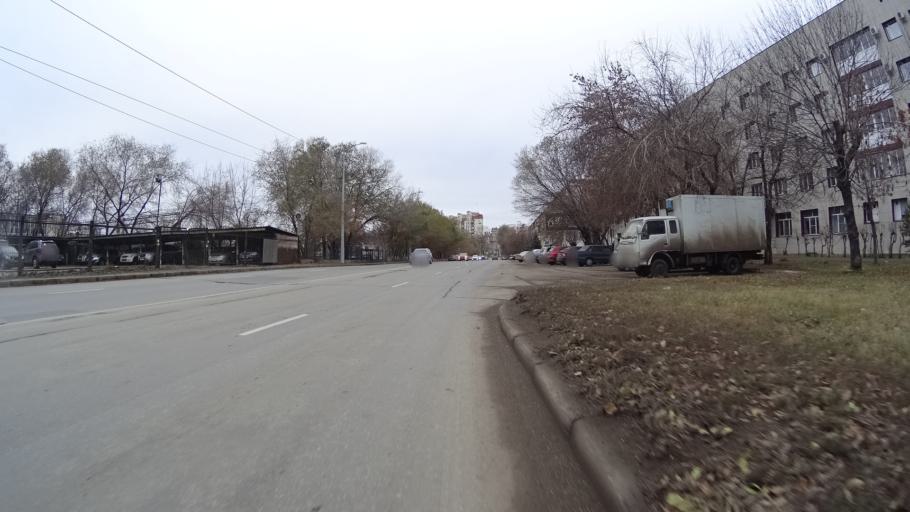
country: RU
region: Chelyabinsk
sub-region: Gorod Chelyabinsk
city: Chelyabinsk
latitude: 55.1533
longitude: 61.4188
